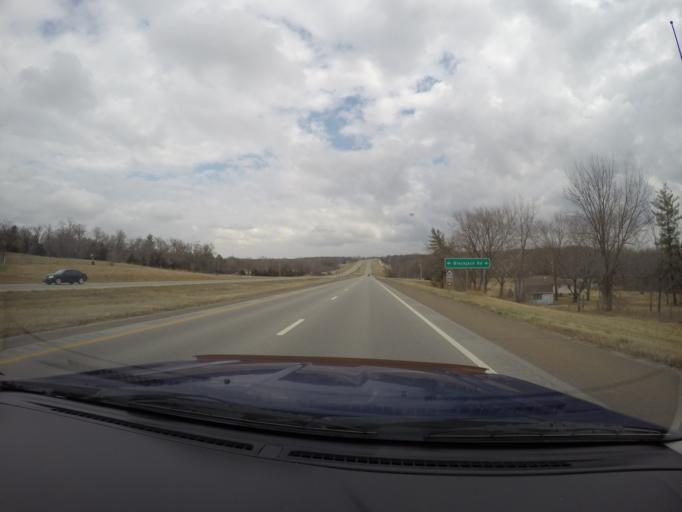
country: US
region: Kansas
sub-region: Pottawatomie County
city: Wamego
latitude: 39.2045
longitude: -96.4277
